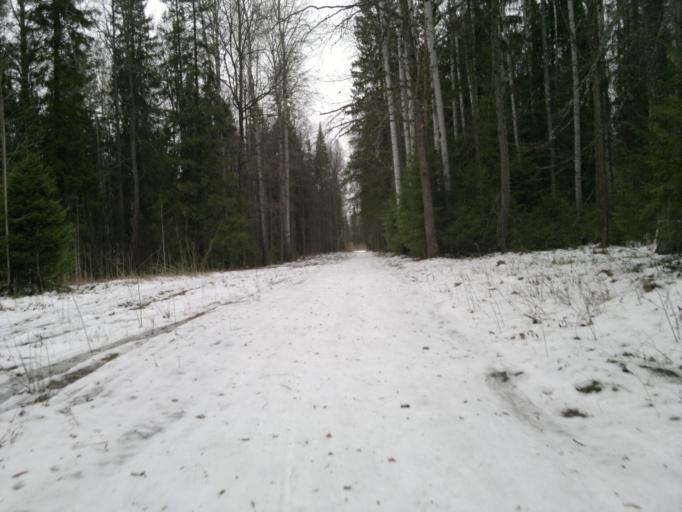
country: RU
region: Mariy-El
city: Yoshkar-Ola
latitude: 56.5926
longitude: 47.9676
